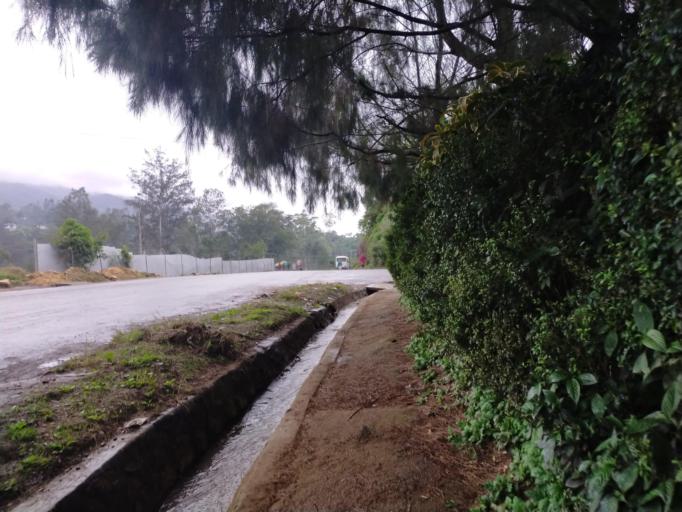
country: PG
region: Southern Highlands
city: Mendi
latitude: -6.1328
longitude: 143.6543
